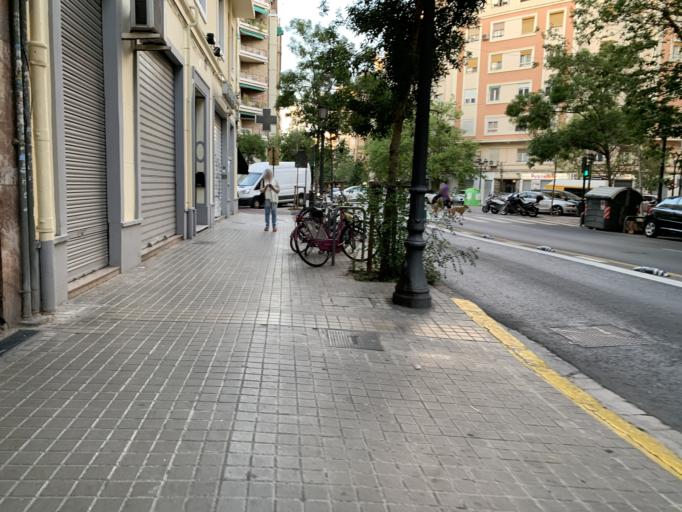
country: ES
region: Valencia
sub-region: Provincia de Valencia
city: Valencia
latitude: 39.4620
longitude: -0.3663
